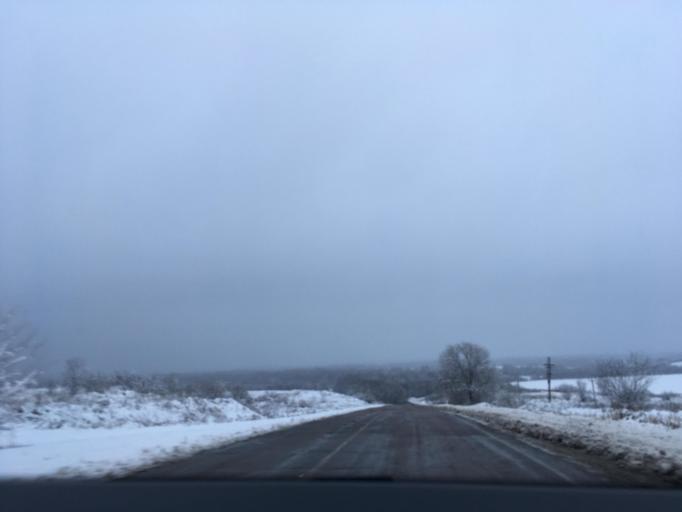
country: RU
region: Voronezj
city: Mitrofanovka
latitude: 50.1356
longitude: 39.9825
